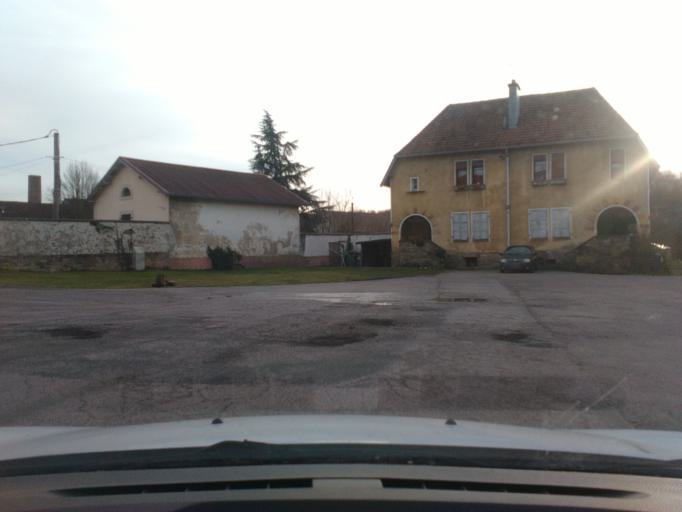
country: FR
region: Lorraine
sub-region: Departement des Vosges
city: Rambervillers
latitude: 48.3357
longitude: 6.6482
